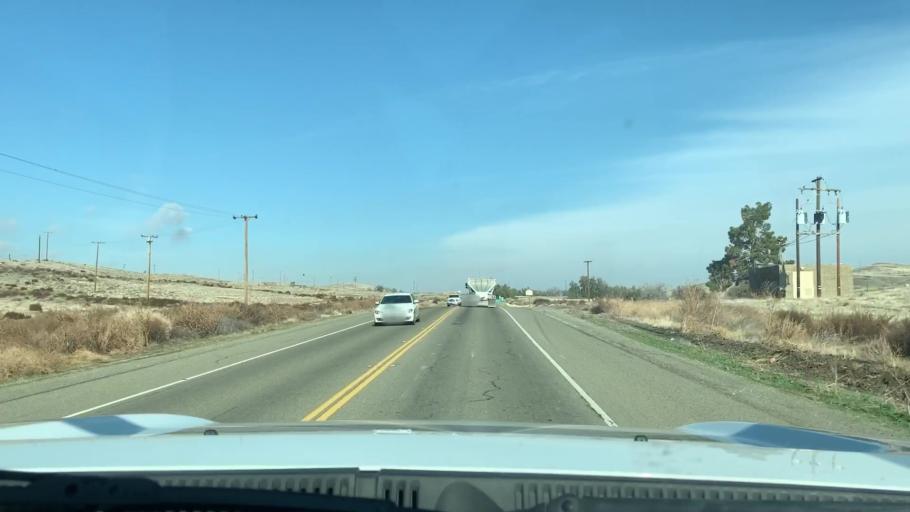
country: US
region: California
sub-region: Fresno County
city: Coalinga
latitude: 36.2423
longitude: -120.3149
